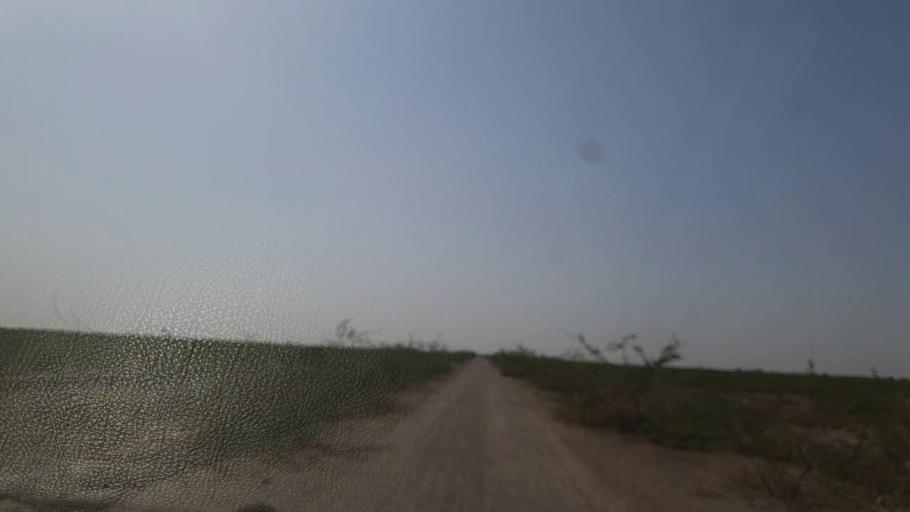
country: PK
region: Sindh
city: Naukot
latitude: 24.5925
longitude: 69.3042
